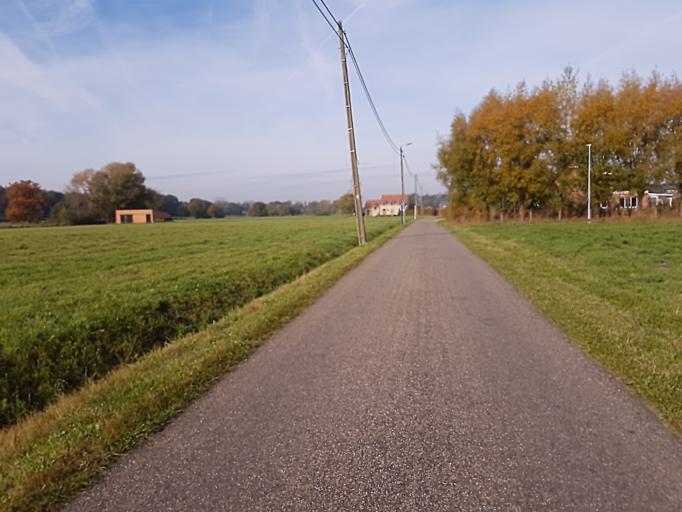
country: BE
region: Flanders
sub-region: Provincie Antwerpen
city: Sint-Katelijne-Waver
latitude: 51.0715
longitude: 4.5677
